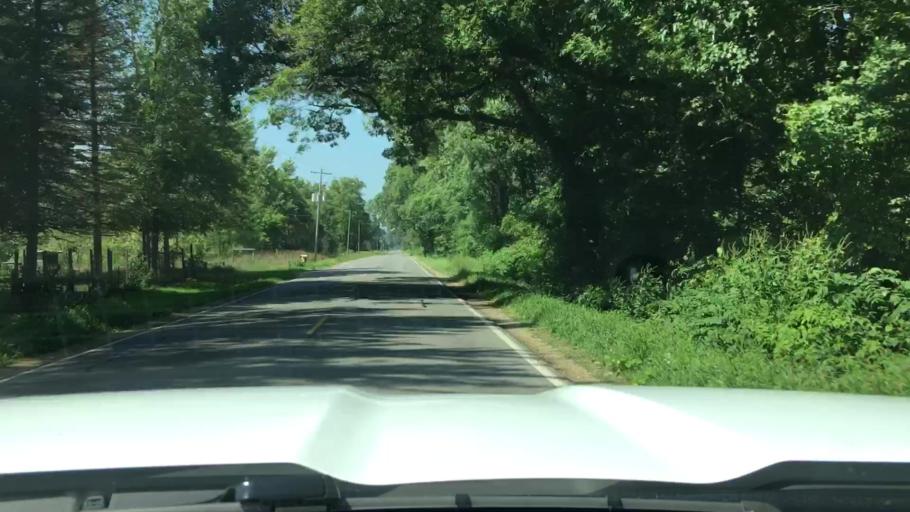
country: US
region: Michigan
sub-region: Saint Joseph County
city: Three Rivers
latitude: 41.9985
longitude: -85.6055
